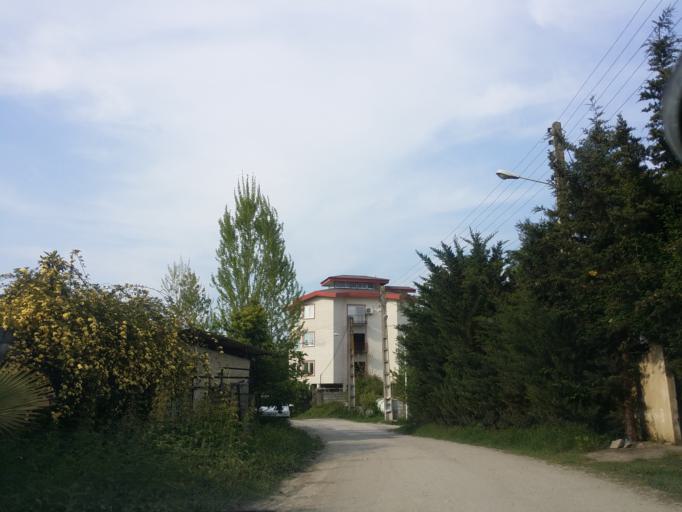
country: IR
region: Mazandaran
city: Chalus
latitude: 36.6837
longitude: 51.3964
